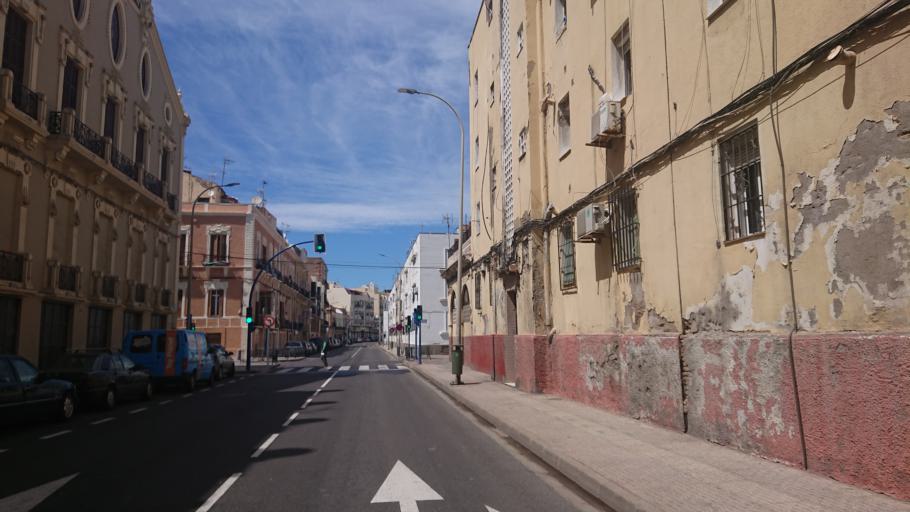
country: ES
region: Melilla
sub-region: Melilla
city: Melilla
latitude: 35.2832
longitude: -2.9411
